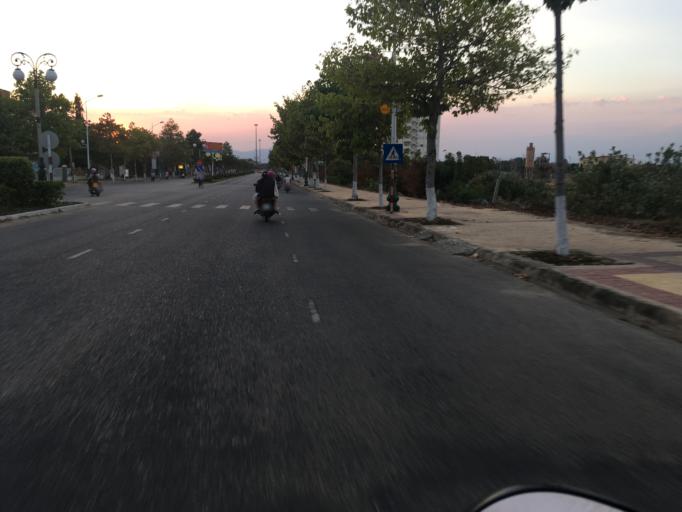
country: VN
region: Ninh Thuan
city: Phan Rang-Thap Cham
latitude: 11.5648
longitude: 109.0046
